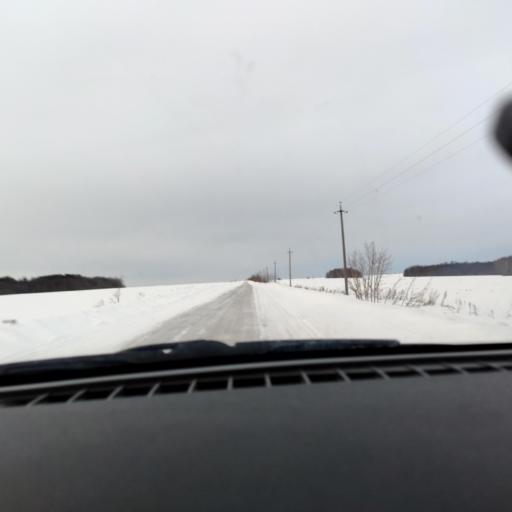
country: RU
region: Bashkortostan
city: Iglino
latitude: 54.7422
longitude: 56.5359
